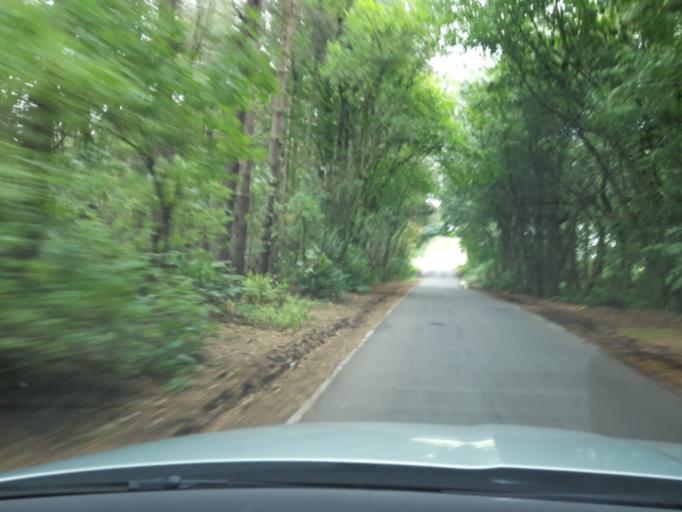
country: GB
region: Scotland
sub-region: West Lothian
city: Broxburn
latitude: 55.9174
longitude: -3.4607
